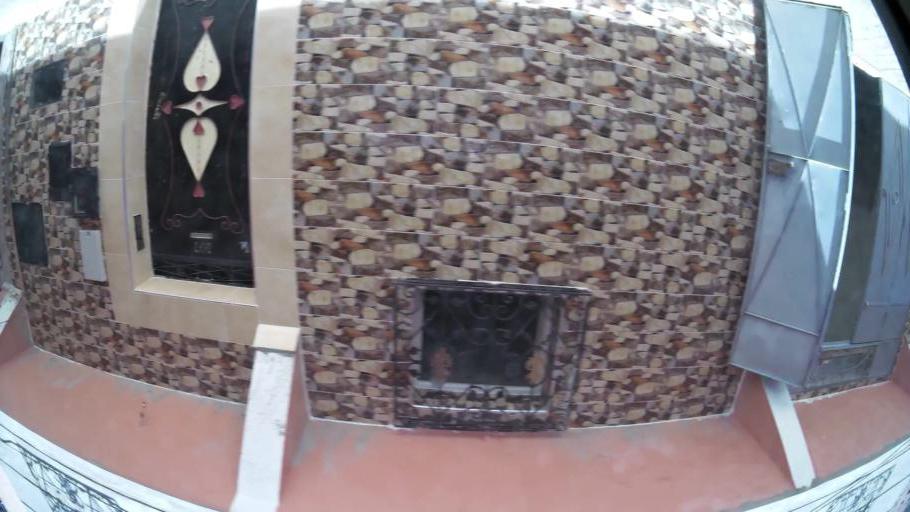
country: MA
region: Marrakech-Tensift-Al Haouz
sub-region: Marrakech
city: Marrakesh
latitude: 31.6575
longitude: -7.9938
